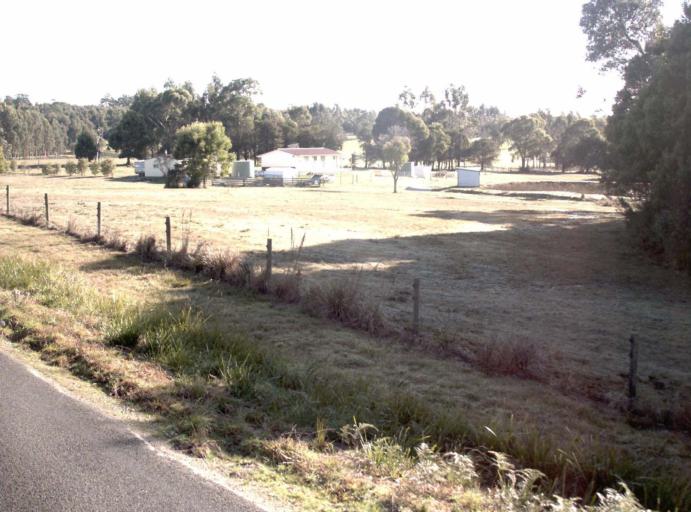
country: AU
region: Tasmania
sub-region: Dorset
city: Bridport
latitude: -41.1021
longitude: 147.1972
